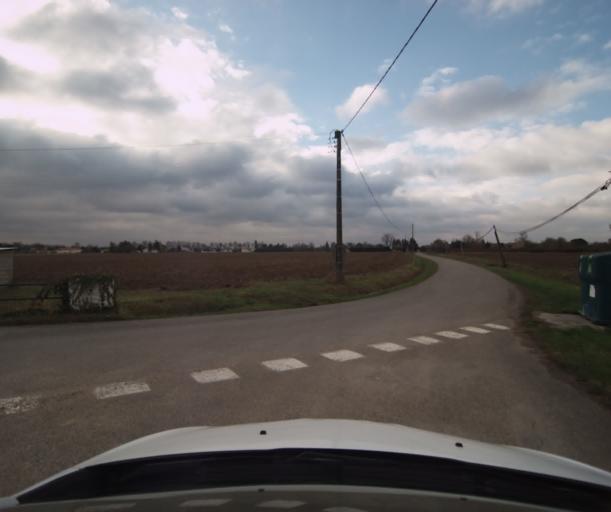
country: FR
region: Midi-Pyrenees
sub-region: Departement du Tarn-et-Garonne
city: Castelsarrasin
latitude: 44.0417
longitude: 1.1292
